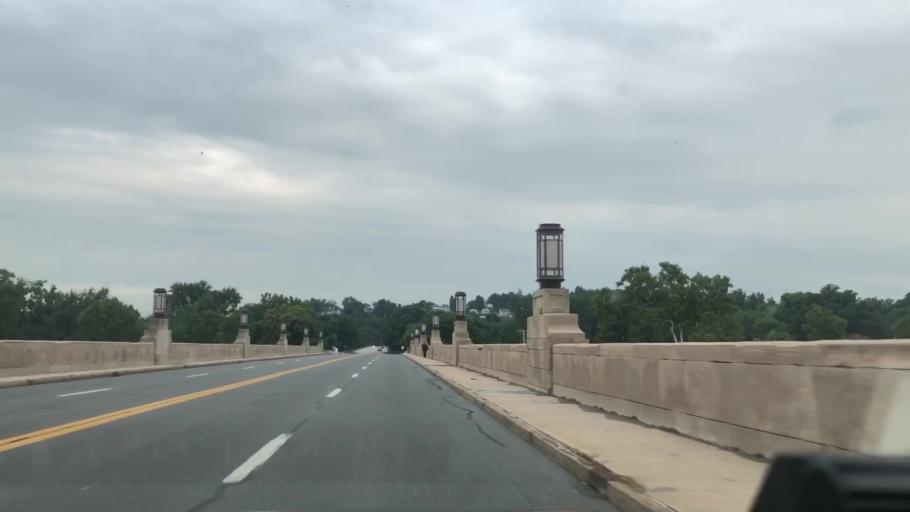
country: US
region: Pennsylvania
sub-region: Dauphin County
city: Harrisburg
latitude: 40.2562
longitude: -76.8851
